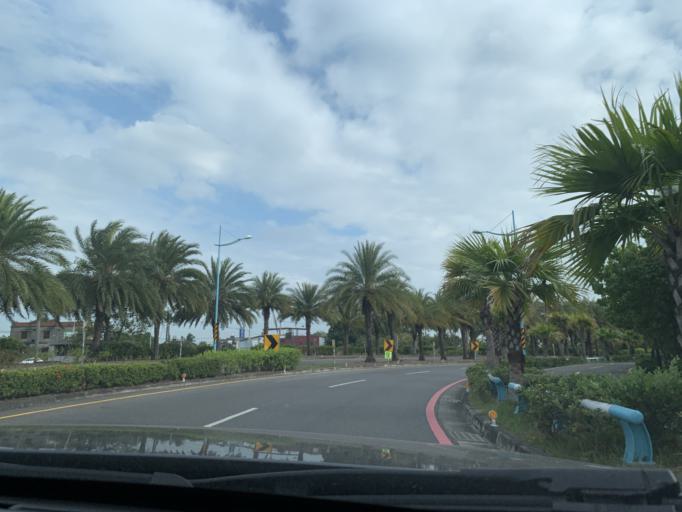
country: TW
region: Taiwan
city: Fengshan
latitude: 22.4554
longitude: 120.4854
